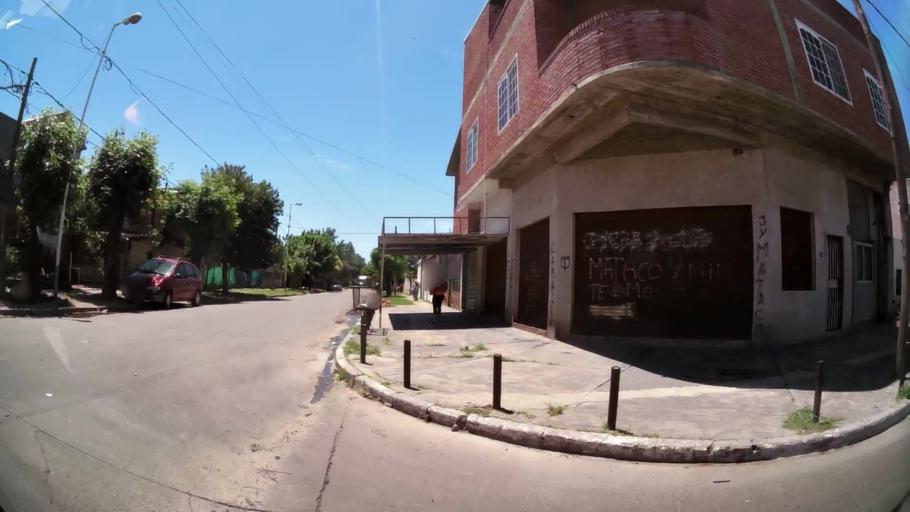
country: AR
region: Buenos Aires
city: Hurlingham
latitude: -34.5094
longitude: -58.7127
